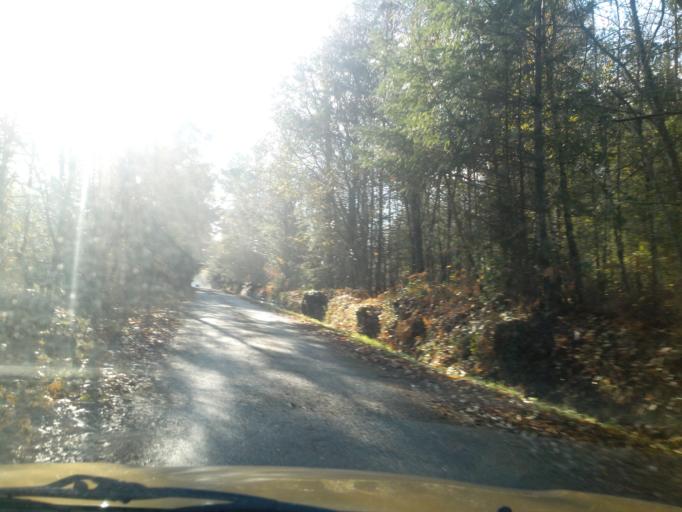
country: FR
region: Brittany
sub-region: Departement du Morbihan
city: Molac
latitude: 47.7273
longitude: -2.4037
